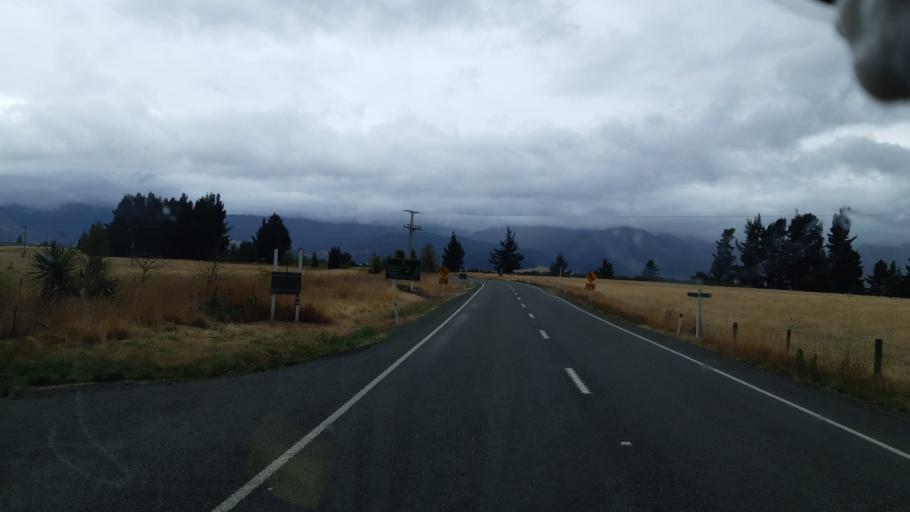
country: NZ
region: Canterbury
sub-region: Hurunui District
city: Amberley
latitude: -42.5849
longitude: 172.7773
